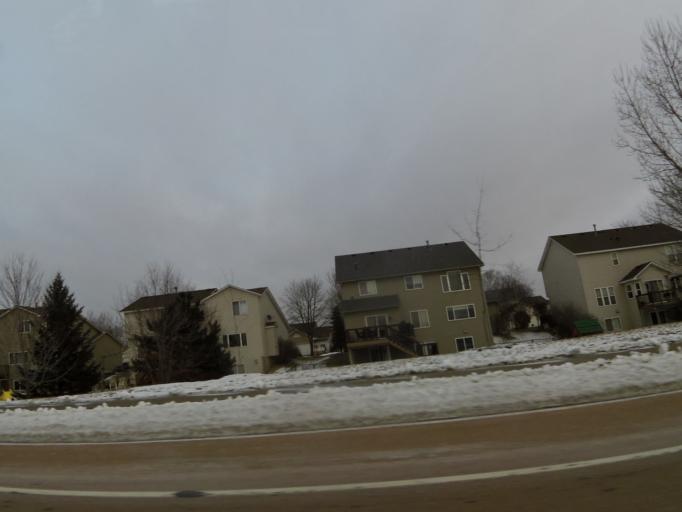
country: US
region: Minnesota
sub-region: Carver County
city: Carver
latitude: 44.7547
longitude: -93.6426
